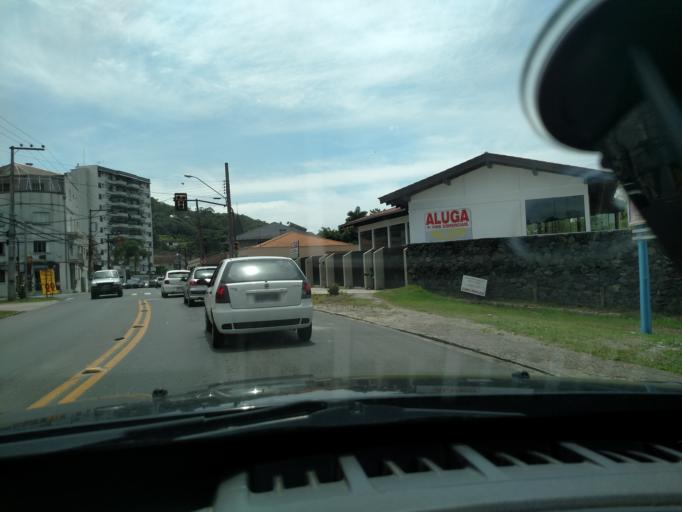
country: BR
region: Santa Catarina
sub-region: Blumenau
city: Blumenau
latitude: -26.9145
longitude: -49.0605
